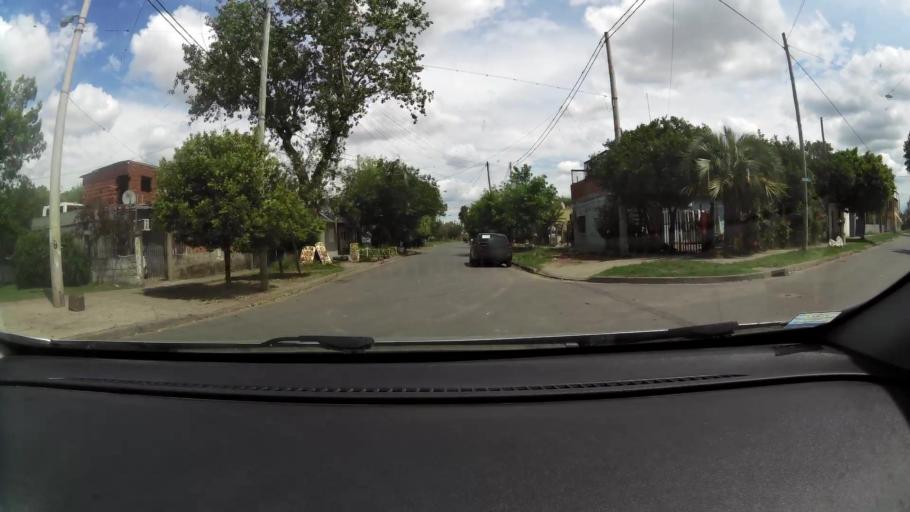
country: AR
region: Santa Fe
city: Gobernador Galvez
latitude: -33.0130
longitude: -60.6382
